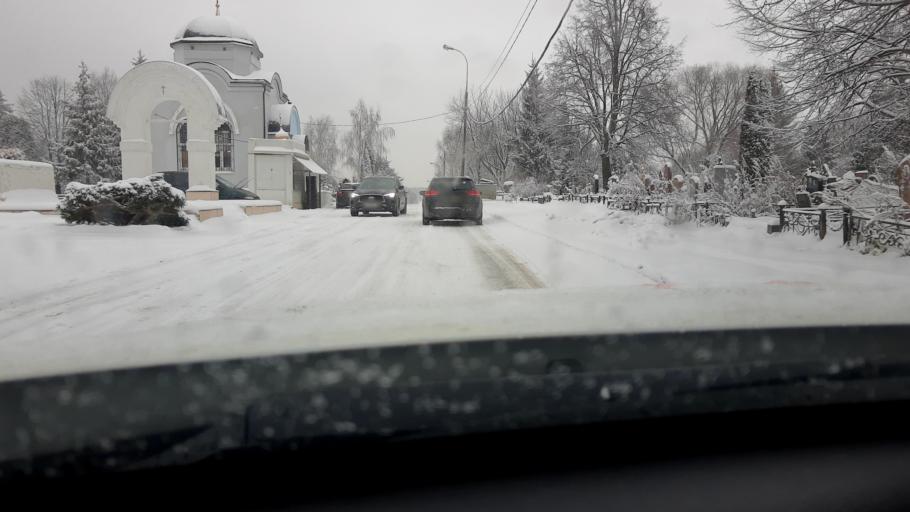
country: RU
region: Moskovskaya
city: Krasnogorsk
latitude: 55.8725
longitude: 37.3476
